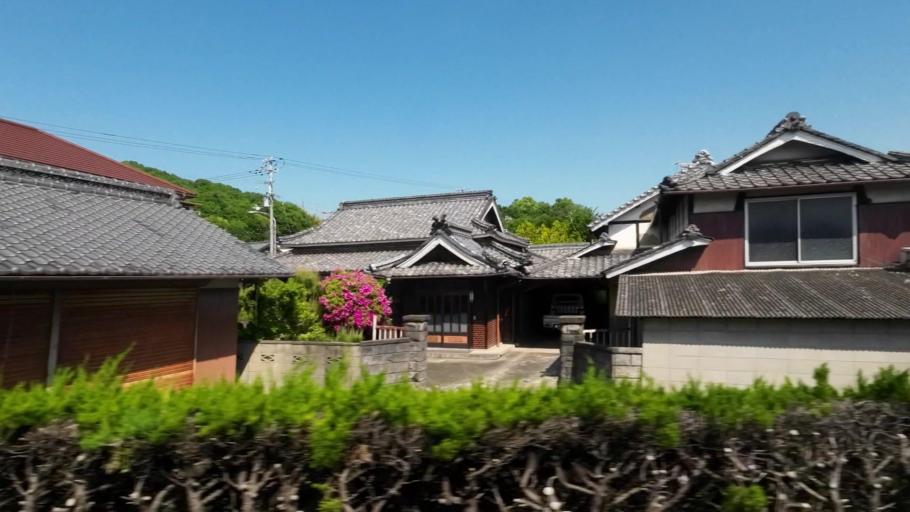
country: JP
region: Kagawa
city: Tadotsu
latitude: 34.2555
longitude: 133.7453
